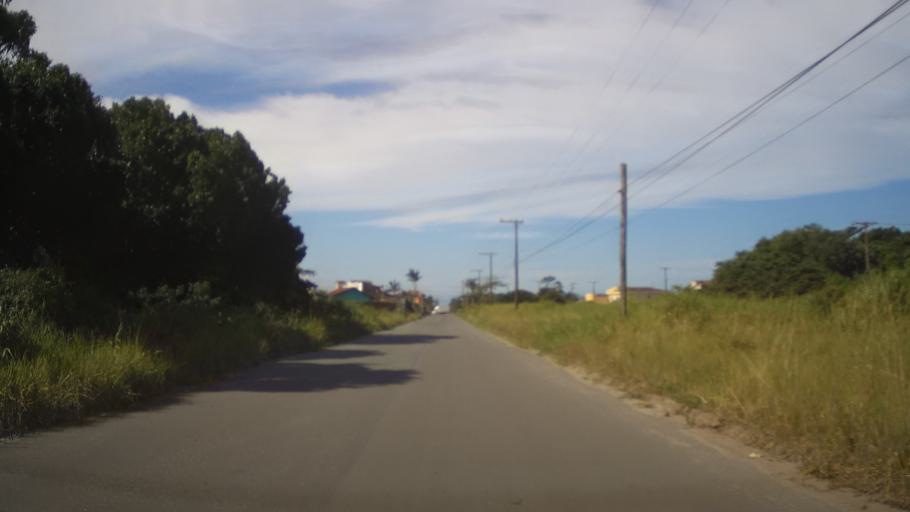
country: BR
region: Sao Paulo
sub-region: Itanhaem
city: Itanhaem
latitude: -24.2152
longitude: -46.8531
